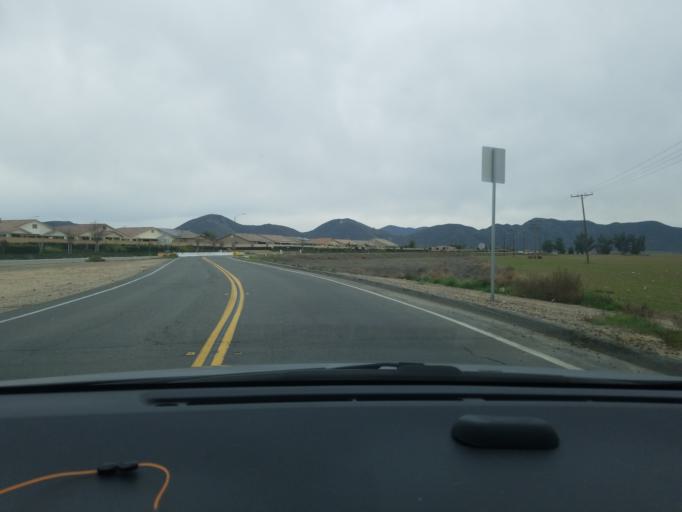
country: US
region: California
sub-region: Riverside County
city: Green Acres
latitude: 33.7242
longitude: -117.0326
